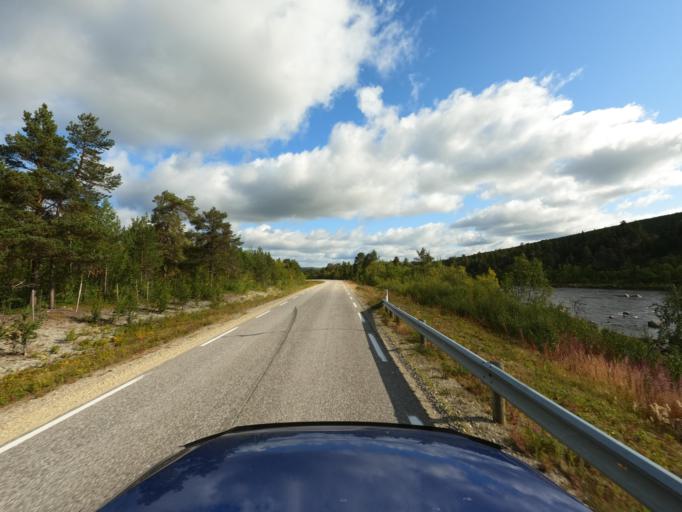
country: NO
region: Finnmark Fylke
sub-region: Karasjok
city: Karasjohka
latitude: 69.4282
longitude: 24.9494
